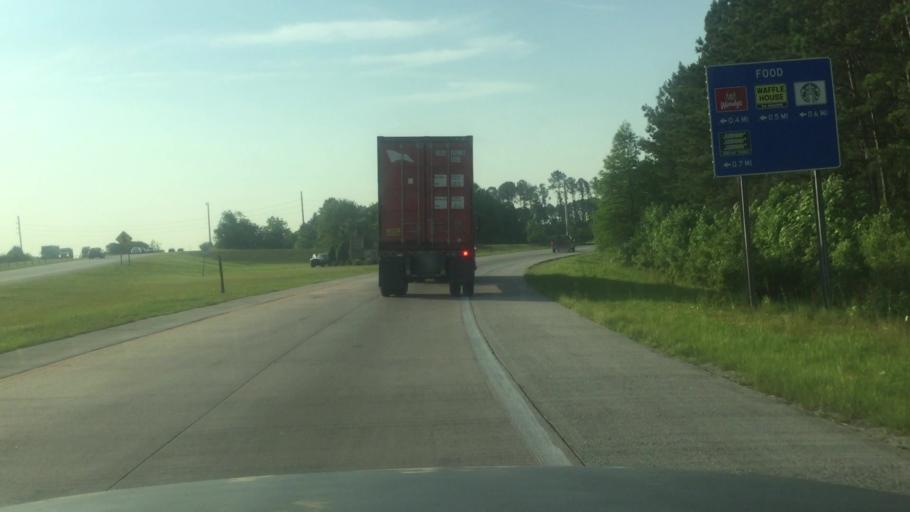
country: US
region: South Carolina
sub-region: Charleston County
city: Mount Pleasant
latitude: 32.8410
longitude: -79.8660
